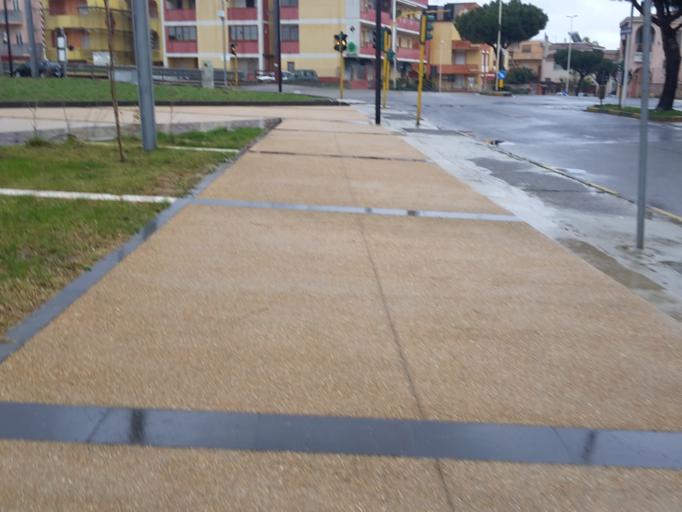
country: IT
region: Sardinia
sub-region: Provincia di Cagliari
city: Monserrato
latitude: 39.2636
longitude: 9.1424
